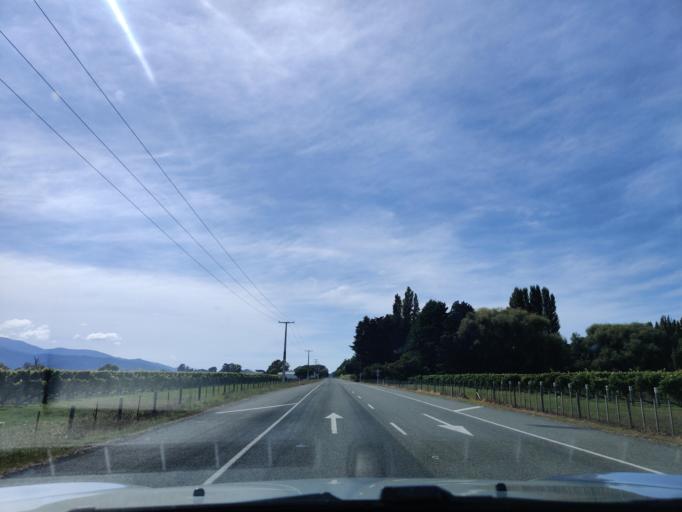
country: NZ
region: Marlborough
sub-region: Marlborough District
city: Blenheim
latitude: -41.4716
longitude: 173.9024
